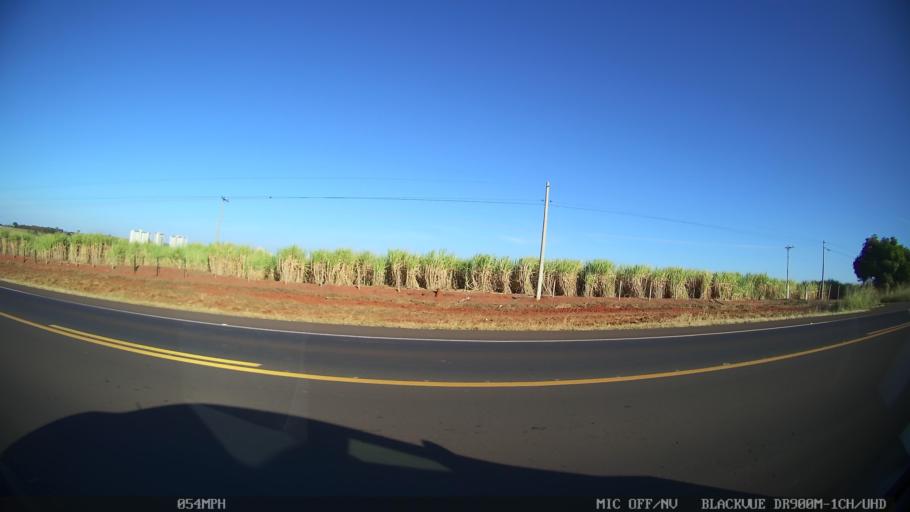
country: BR
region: Sao Paulo
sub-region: Olimpia
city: Olimpia
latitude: -20.6975
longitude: -48.9323
